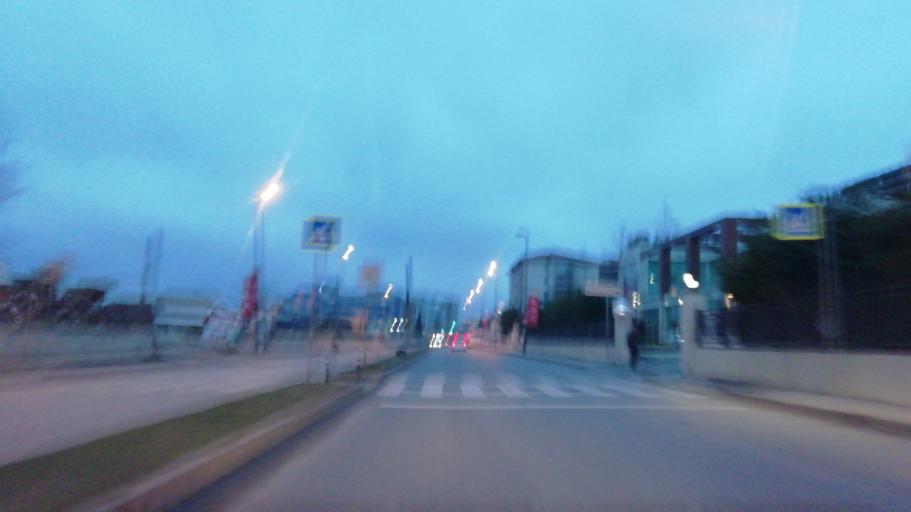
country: TR
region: Istanbul
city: Mahmutbey
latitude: 41.0131
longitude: 28.8181
